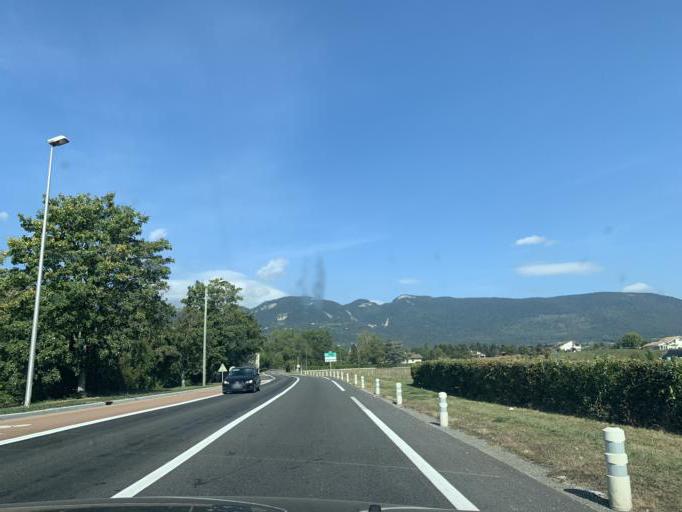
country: FR
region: Rhone-Alpes
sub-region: Departement de l'Ain
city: Cessy
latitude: 46.3189
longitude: 6.0640
